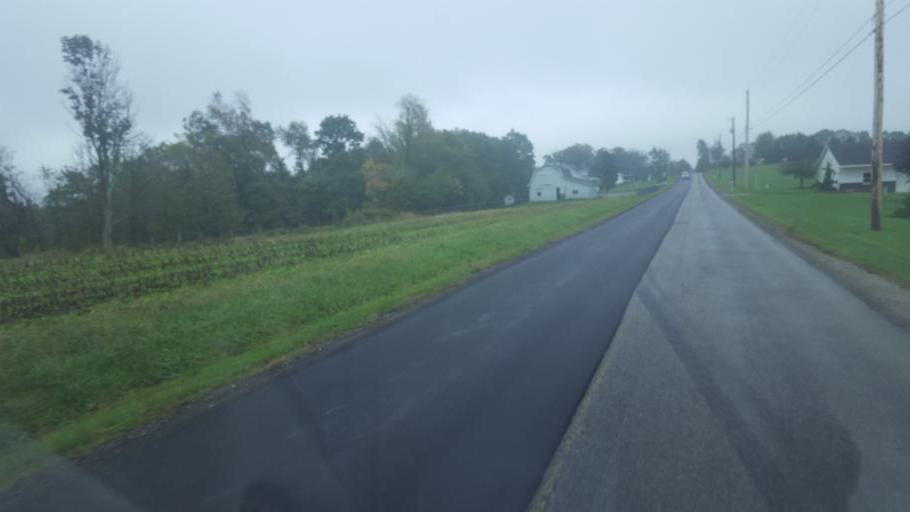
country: US
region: Ohio
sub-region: Tuscarawas County
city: Sugarcreek
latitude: 40.5747
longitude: -81.7273
